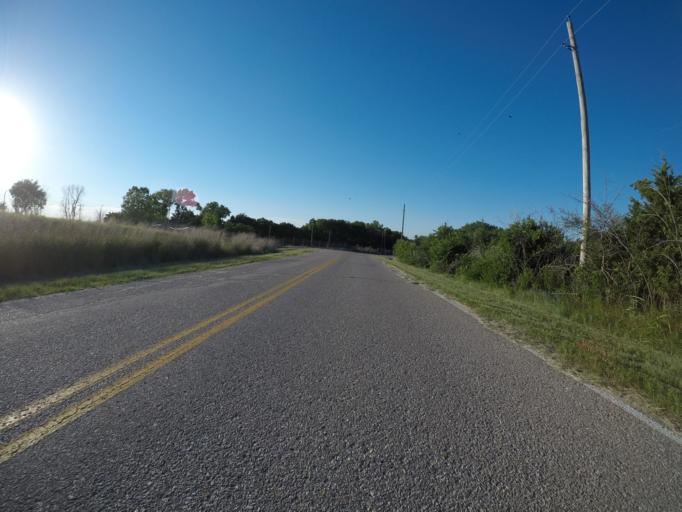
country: US
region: Kansas
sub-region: Riley County
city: Ogden
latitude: 39.1306
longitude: -96.7198
